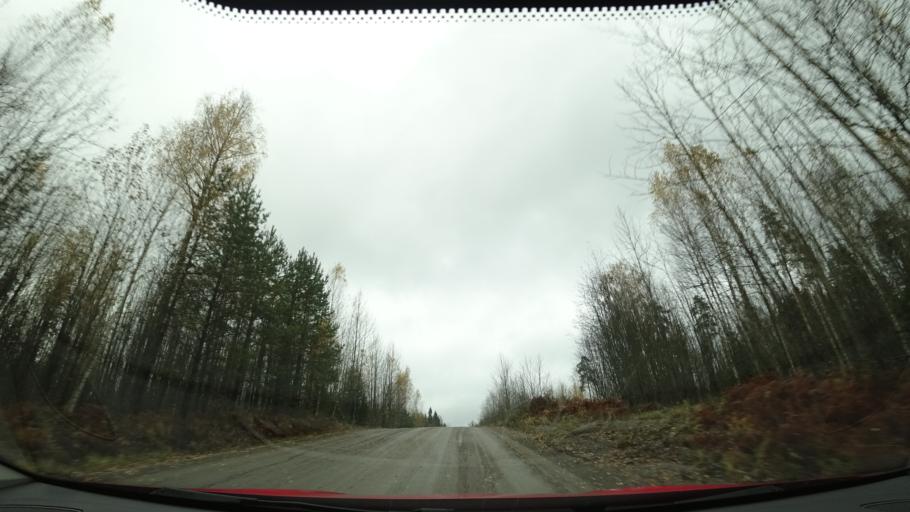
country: FI
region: Uusimaa
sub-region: Helsinki
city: Sibbo
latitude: 60.2977
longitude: 25.1996
